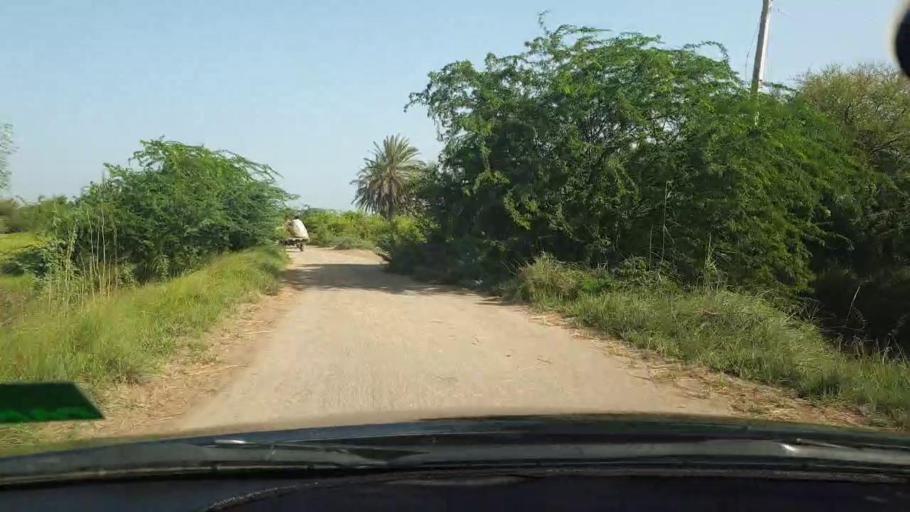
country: PK
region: Sindh
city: Tando Bago
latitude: 24.7173
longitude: 68.9913
